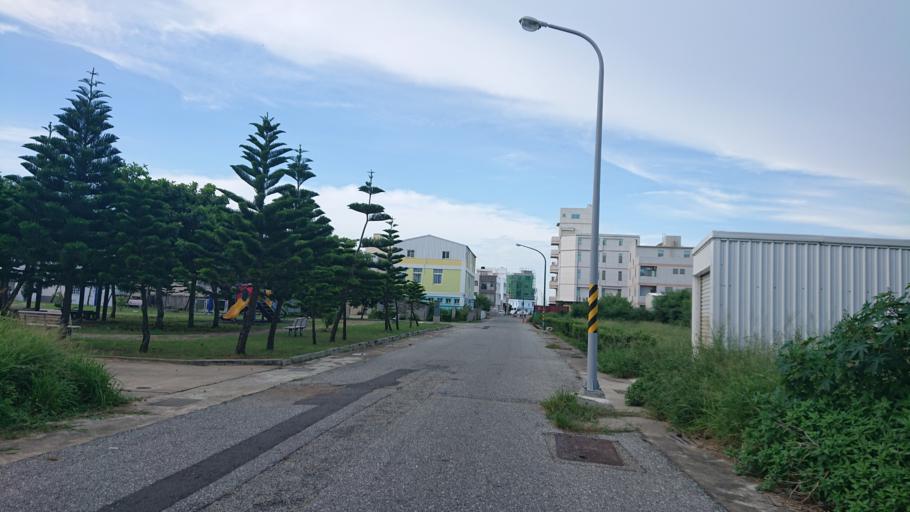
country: TW
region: Taiwan
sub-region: Penghu
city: Ma-kung
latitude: 23.5222
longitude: 119.6024
